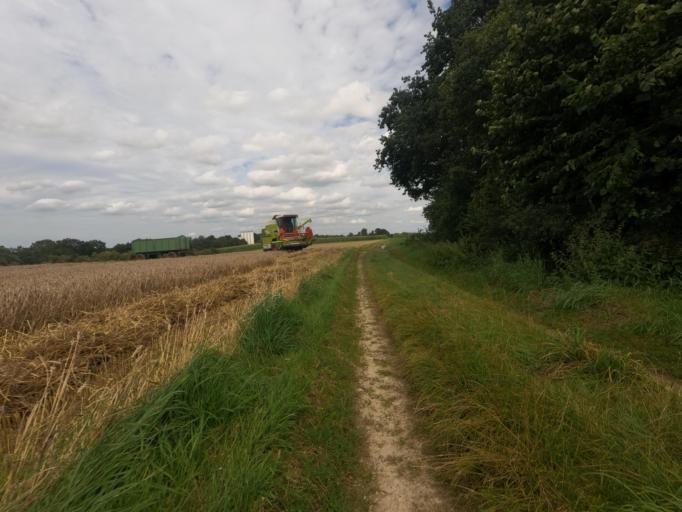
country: DE
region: North Rhine-Westphalia
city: Geilenkirchen
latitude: 50.9821
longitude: 6.1653
